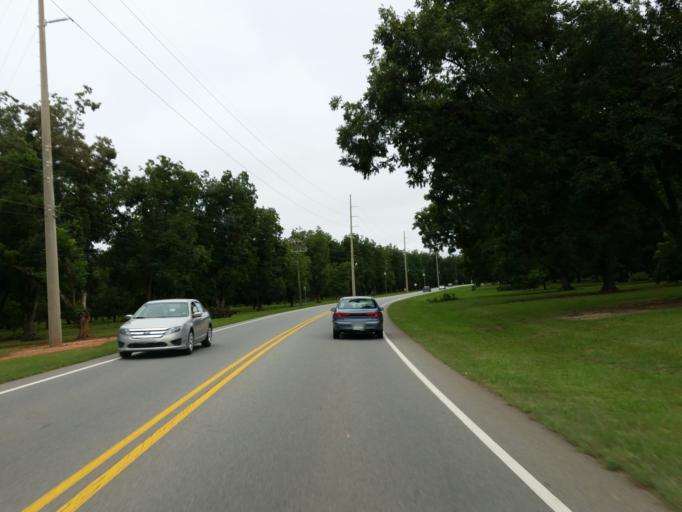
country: US
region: Georgia
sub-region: Peach County
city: Fort Valley
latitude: 32.5737
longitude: -83.8920
